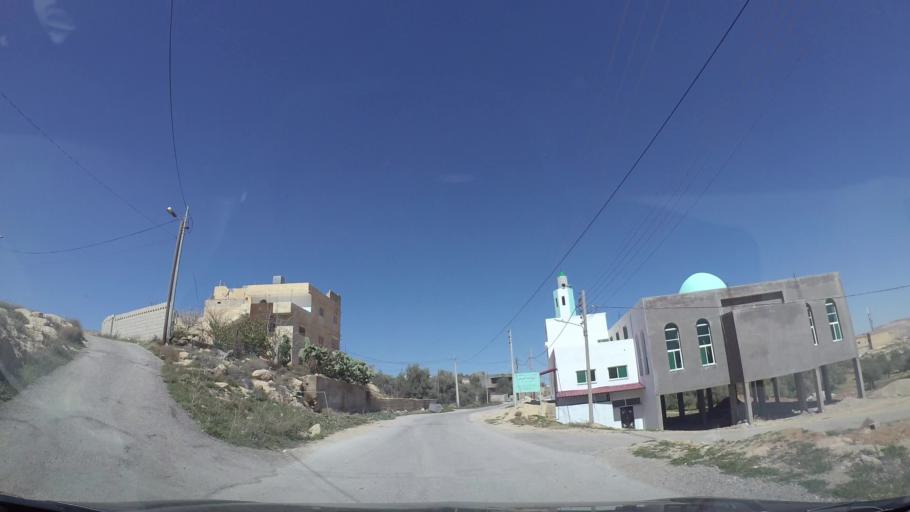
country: JO
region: Tafielah
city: At Tafilah
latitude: 30.8261
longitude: 35.5801
